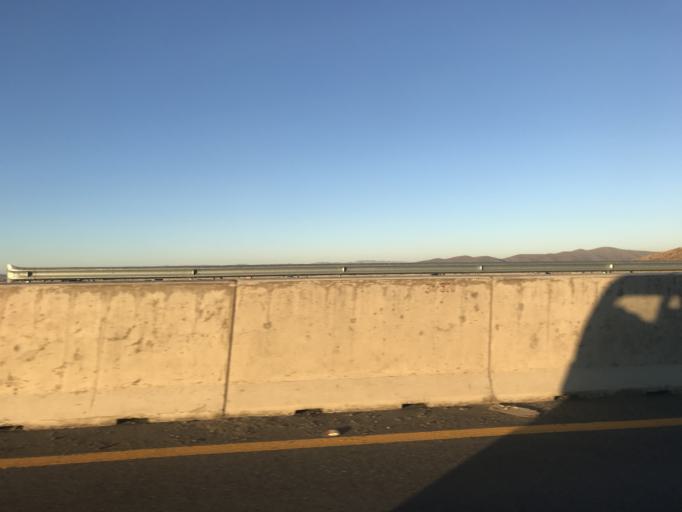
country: BO
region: La Paz
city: Batallas
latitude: -16.3055
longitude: -68.4781
